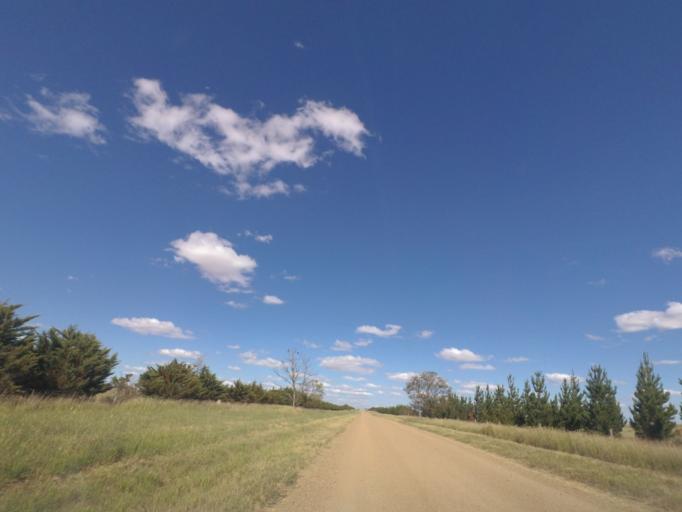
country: AU
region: Victoria
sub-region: Hume
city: Sunbury
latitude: -37.4578
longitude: 144.7815
